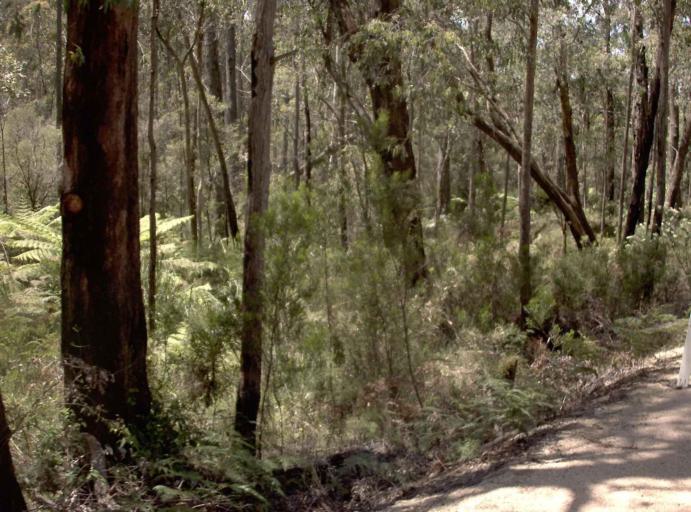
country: AU
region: New South Wales
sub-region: Bombala
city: Bombala
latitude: -37.6356
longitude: 148.8659
